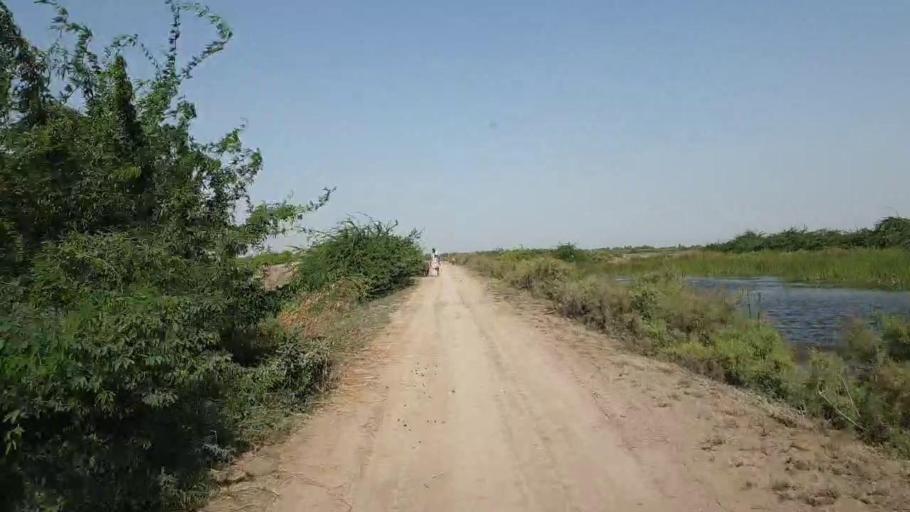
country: PK
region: Sindh
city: Tando Bago
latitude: 24.6589
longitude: 69.0694
